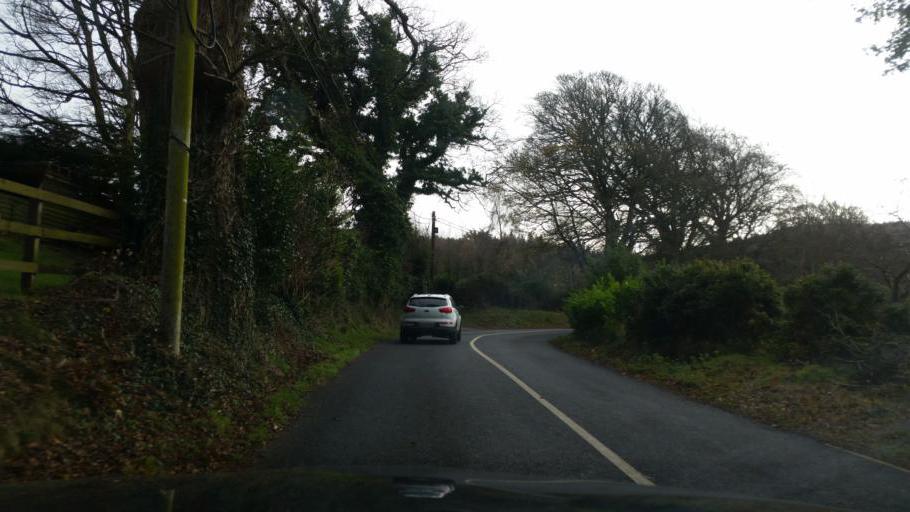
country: IE
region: Leinster
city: Ballyboden
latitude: 53.2501
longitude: -6.3003
